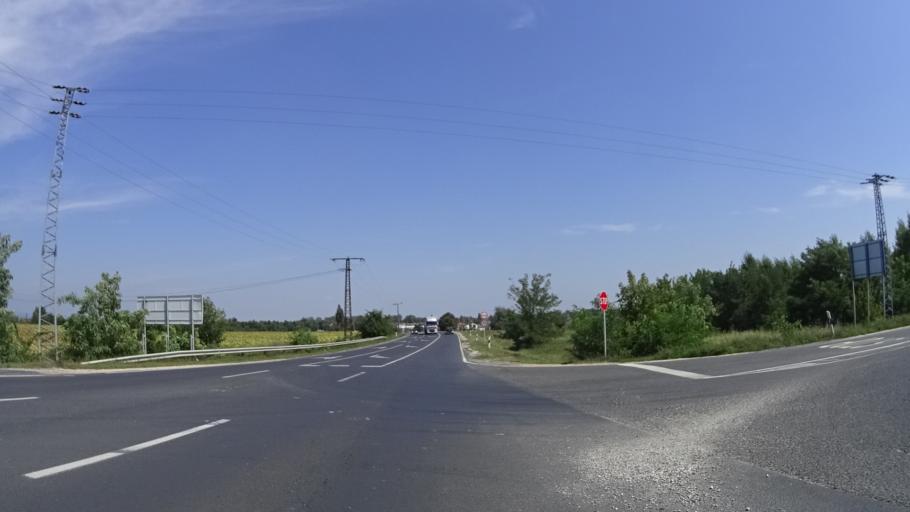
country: HU
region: Fejer
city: Szekesfehervar
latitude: 47.1506
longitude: 18.3967
